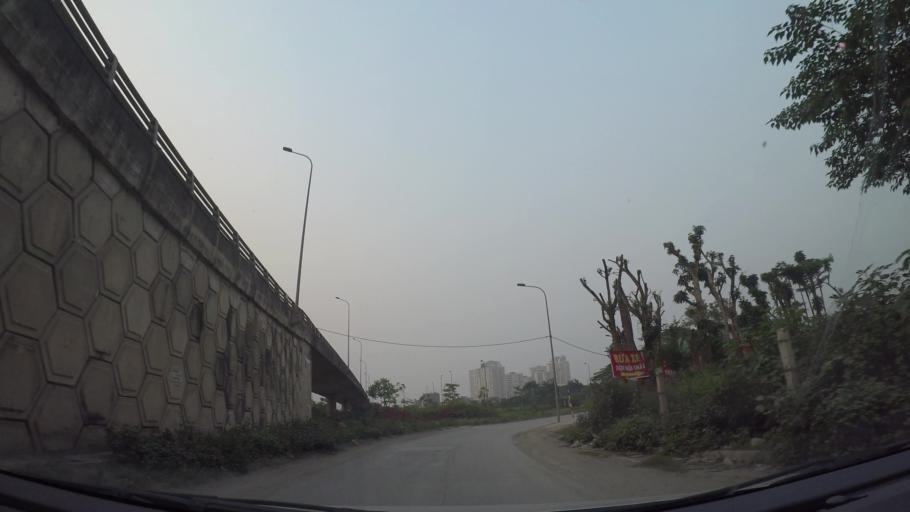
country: VN
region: Ha Noi
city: Cau Dien
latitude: 21.0101
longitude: 105.7206
